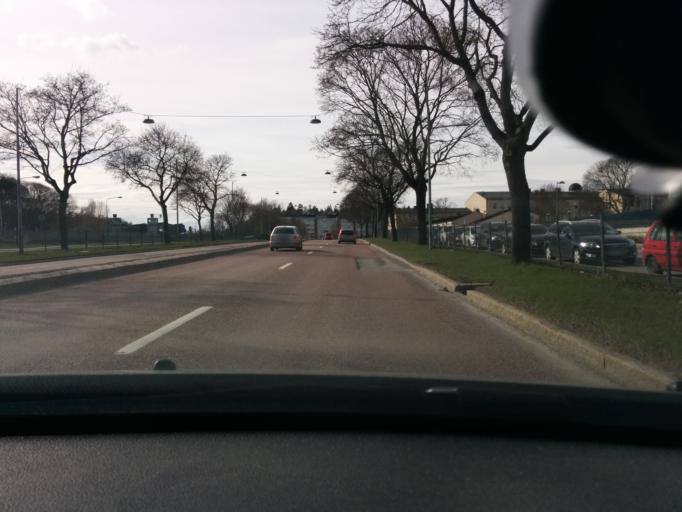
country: SE
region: Stockholm
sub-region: Stockholms Kommun
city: Bromma
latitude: 59.3420
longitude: 17.9280
